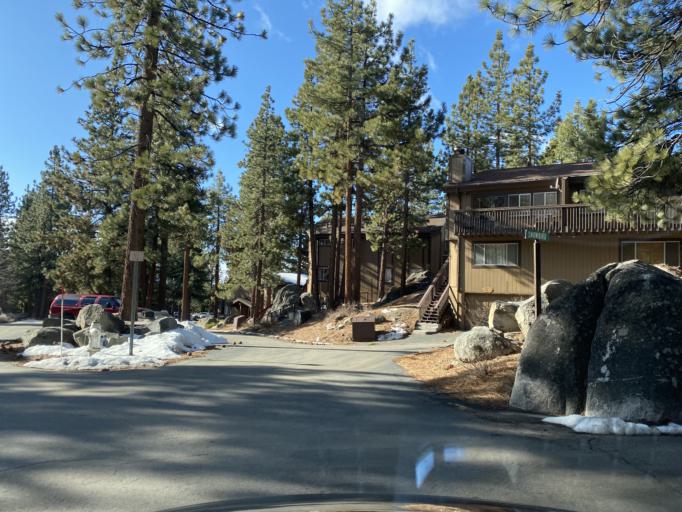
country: US
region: Nevada
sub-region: Douglas County
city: Kingsbury
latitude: 38.9786
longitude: -119.9328
